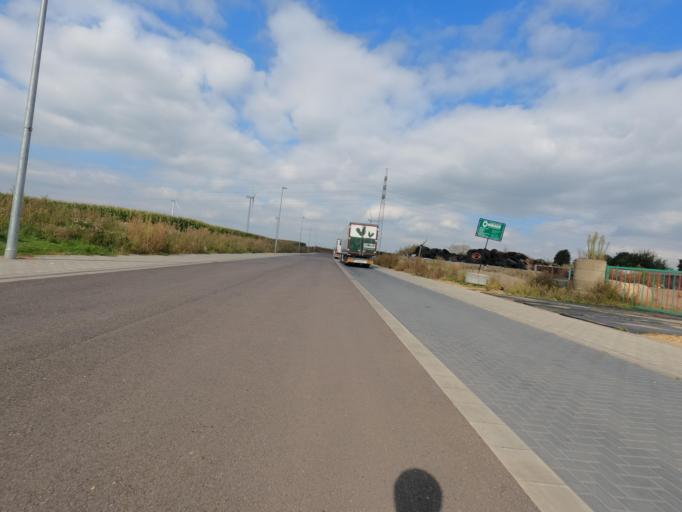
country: DE
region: North Rhine-Westphalia
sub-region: Regierungsbezirk Koln
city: Ubach-Palenberg
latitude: 50.9264
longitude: 6.1350
